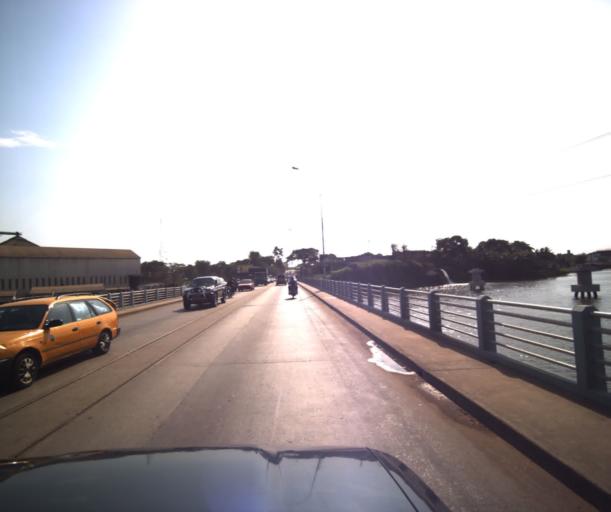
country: CM
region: Littoral
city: Bonaberi
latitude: 4.0717
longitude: 9.6911
